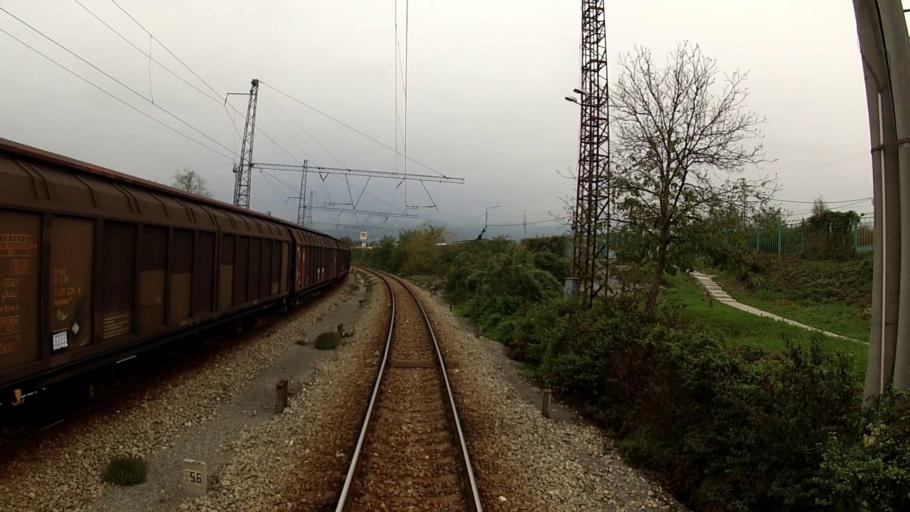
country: RS
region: Central Serbia
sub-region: Pirotski Okrug
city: Dimitrovgrad
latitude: 42.9947
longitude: 22.8423
